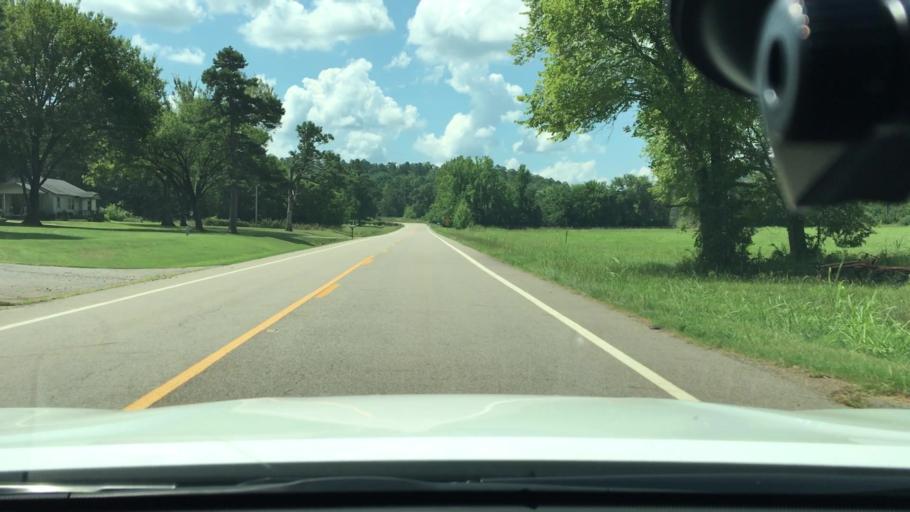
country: US
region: Arkansas
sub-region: Logan County
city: Paris
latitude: 35.2612
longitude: -93.6833
